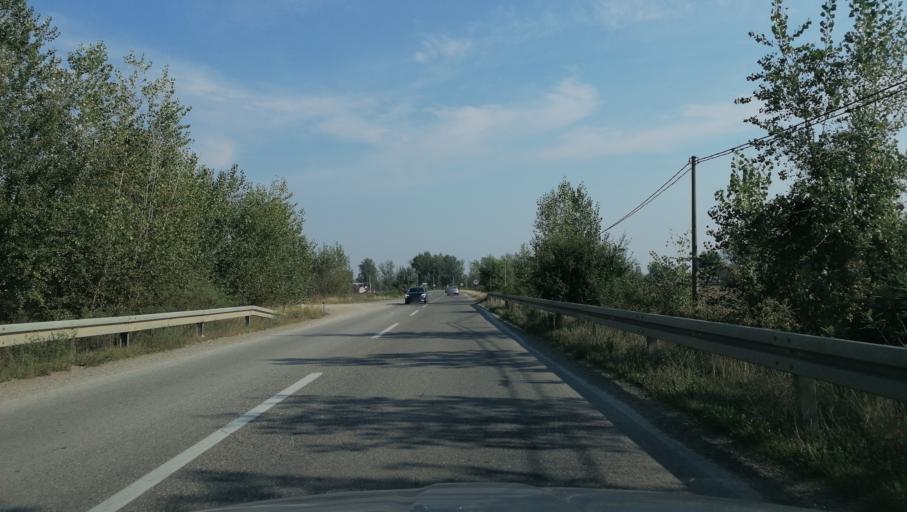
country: RS
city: Badovinci
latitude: 44.7761
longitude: 19.3299
